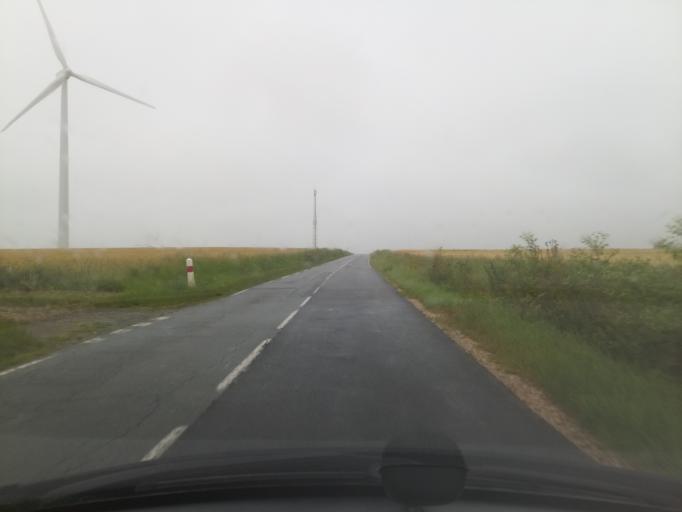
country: FR
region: Poitou-Charentes
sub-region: Departement de la Charente-Maritime
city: Saint-Jean-de-Liversay
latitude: 46.2420
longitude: -0.8812
